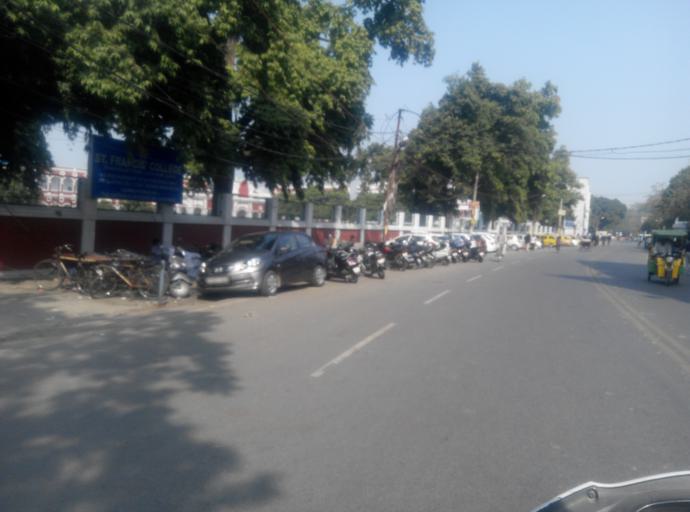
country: IN
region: Uttar Pradesh
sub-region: Lucknow District
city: Lucknow
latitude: 26.8504
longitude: 80.9448
